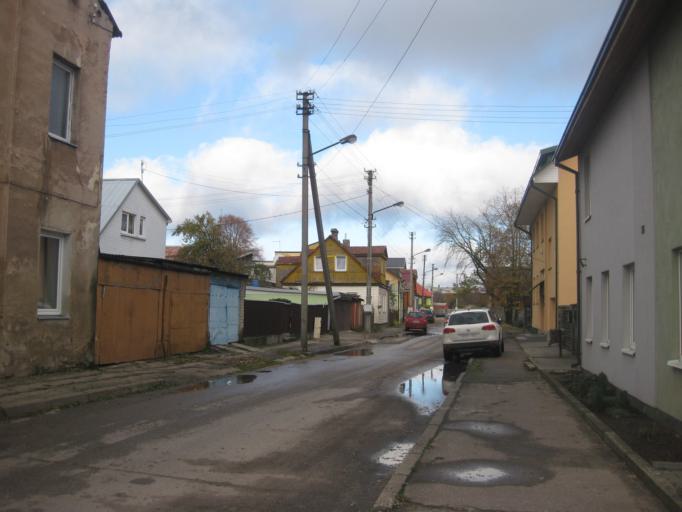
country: LT
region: Kauno apskritis
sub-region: Kaunas
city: Kaunas
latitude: 54.9057
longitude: 23.8891
